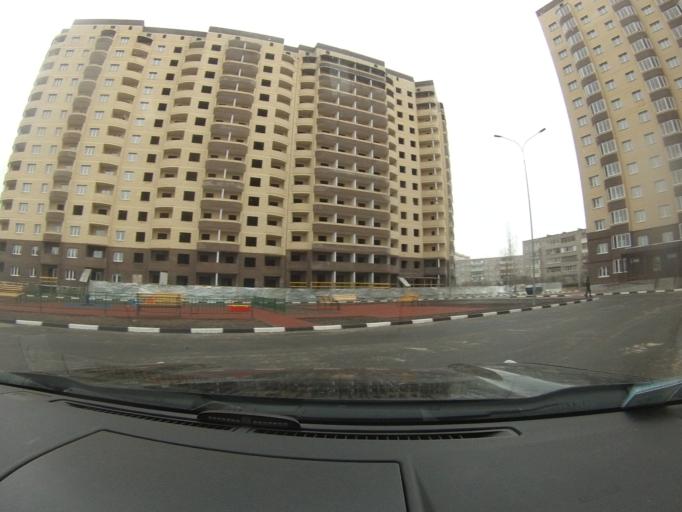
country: RU
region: Moskovskaya
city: Peski
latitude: 55.2719
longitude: 38.7497
